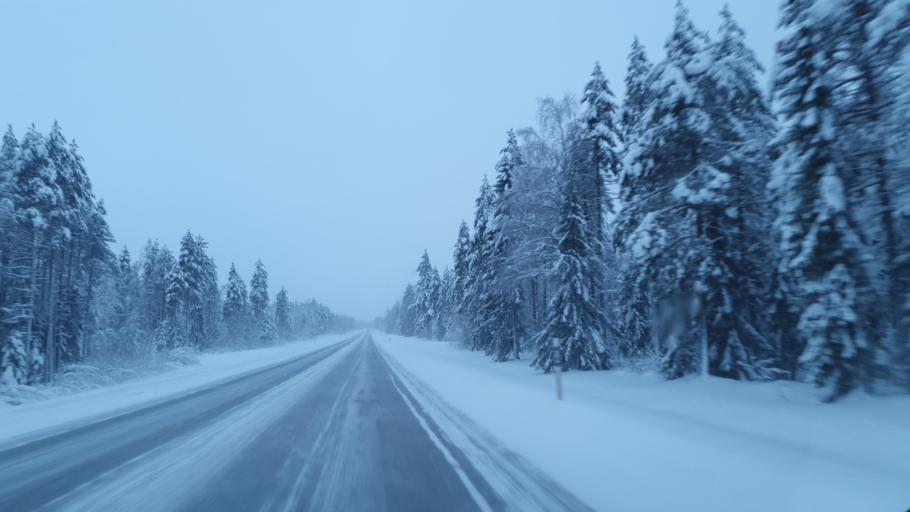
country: FI
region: Kainuu
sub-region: Kajaani
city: Vaala
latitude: 64.5510
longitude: 27.0634
